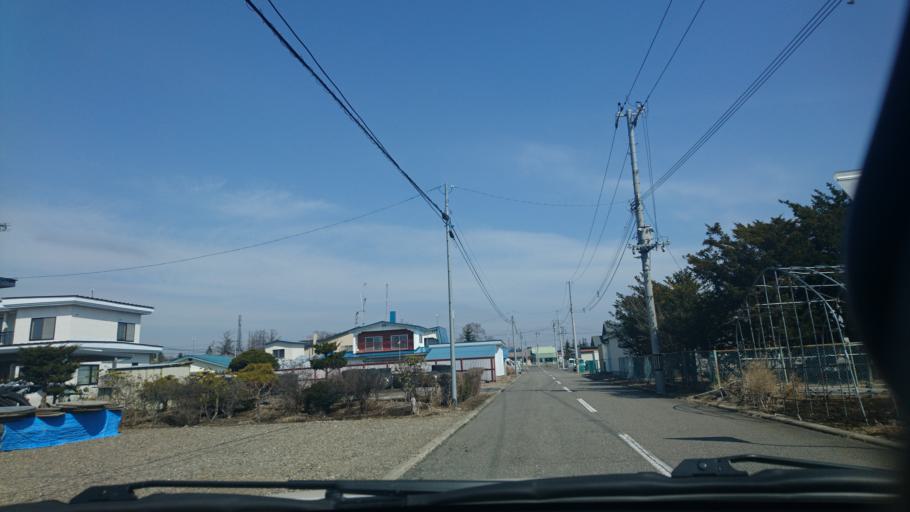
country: JP
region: Hokkaido
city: Otofuke
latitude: 43.0976
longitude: 143.2288
